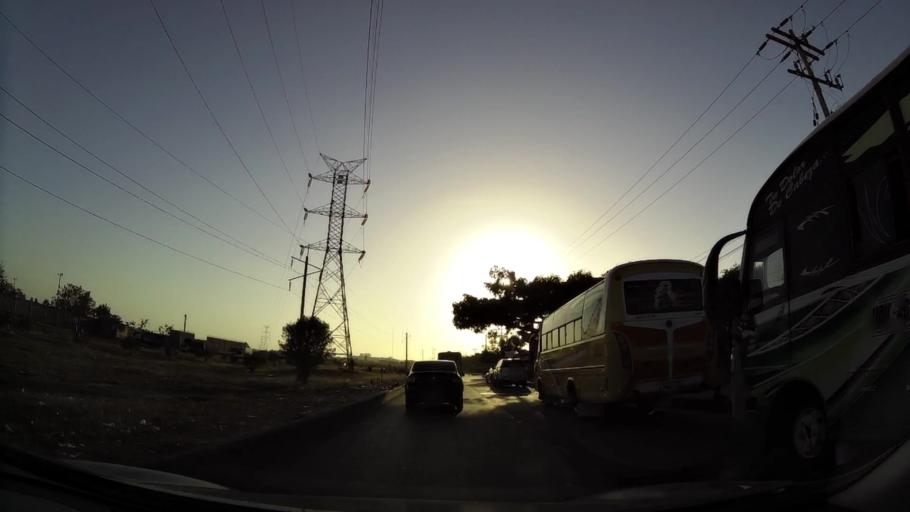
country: CO
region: Bolivar
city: Cartagena
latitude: 10.4067
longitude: -75.4517
